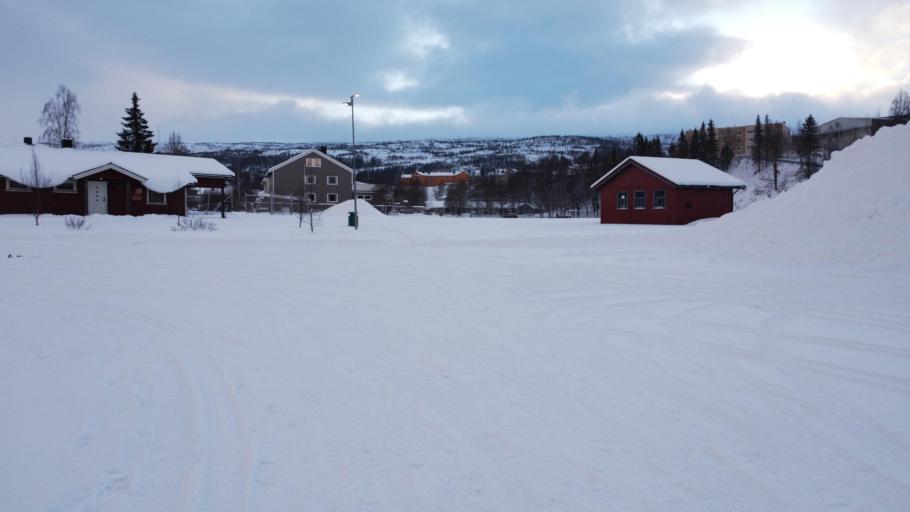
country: NO
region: Nordland
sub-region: Rana
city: Mo i Rana
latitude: 66.3214
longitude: 14.1611
